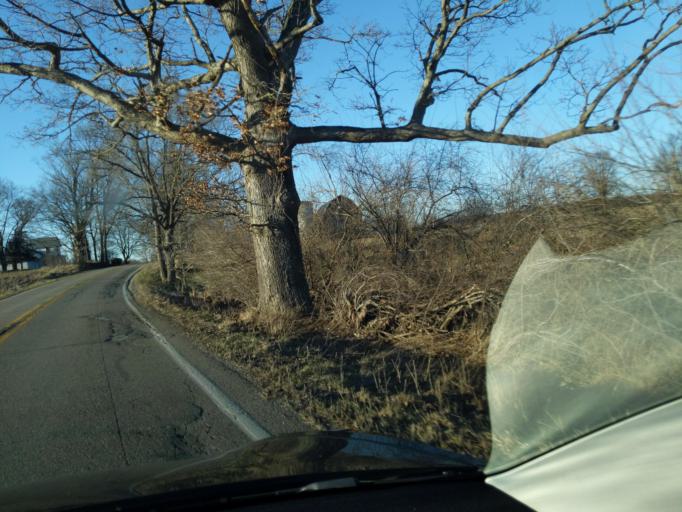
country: US
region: Michigan
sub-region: Livingston County
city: Pinckney
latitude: 42.4418
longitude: -84.0604
